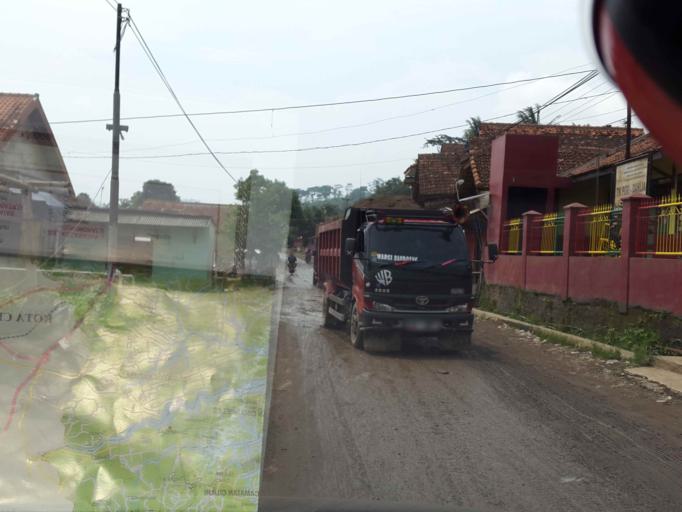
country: ID
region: West Java
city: Padalarang
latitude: -6.8563
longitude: 107.4585
